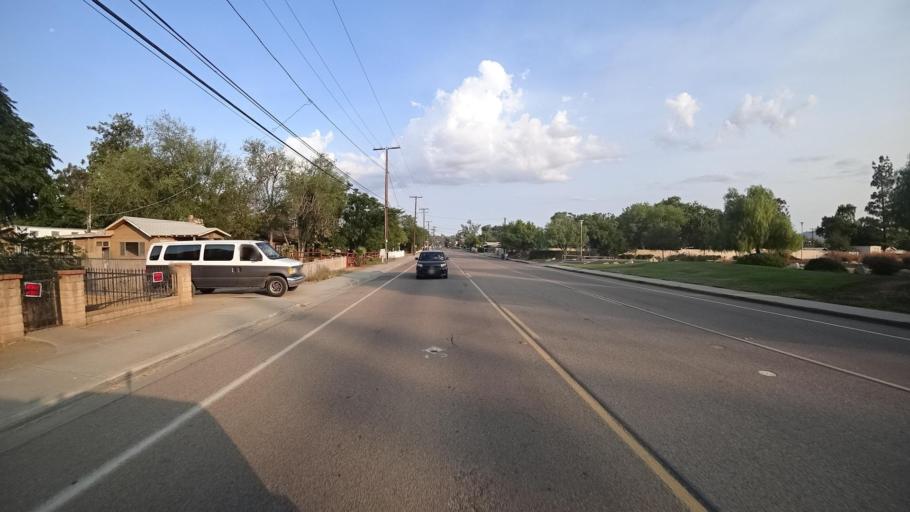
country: US
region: California
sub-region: San Diego County
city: Ramona
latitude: 33.0395
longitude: -116.8667
